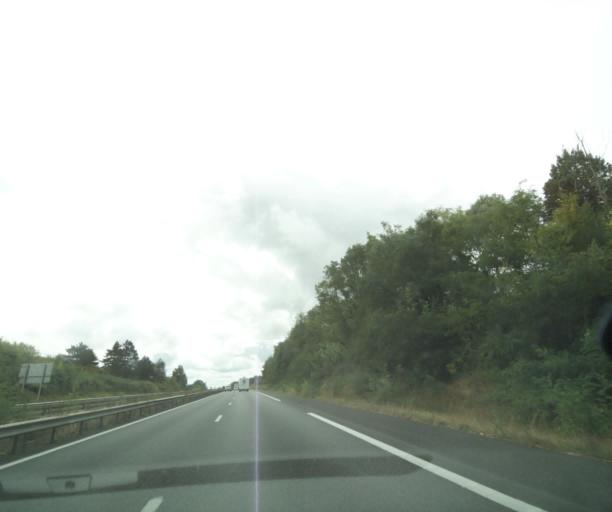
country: FR
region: Poitou-Charentes
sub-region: Departement de la Charente-Maritime
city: Mirambeau
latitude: 45.3520
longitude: -0.5824
